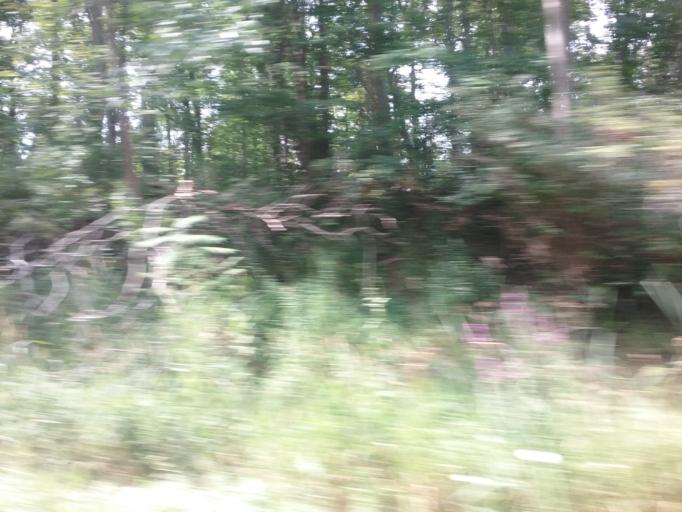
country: US
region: Pennsylvania
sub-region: Tioga County
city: Wellsboro
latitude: 41.7634
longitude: -77.2121
